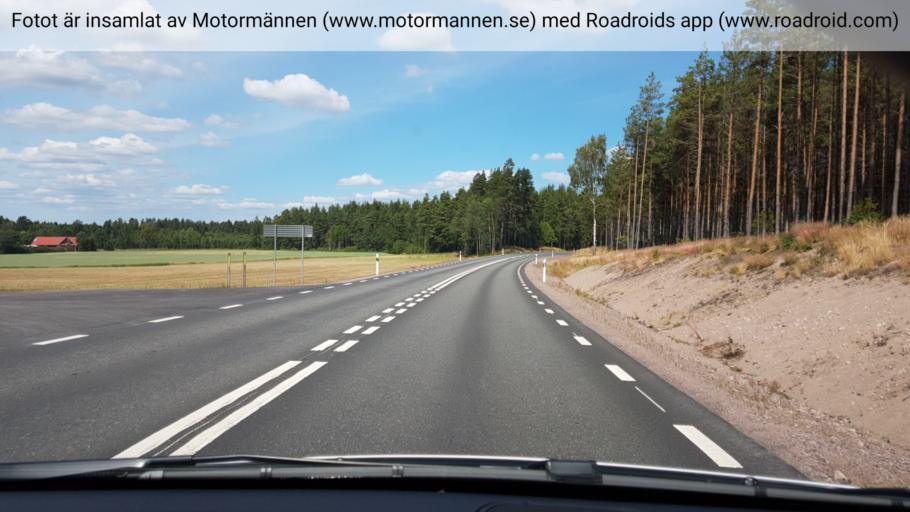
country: SE
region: Vaestra Goetaland
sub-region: Tibro Kommun
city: Tibro
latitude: 58.4556
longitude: 14.1767
